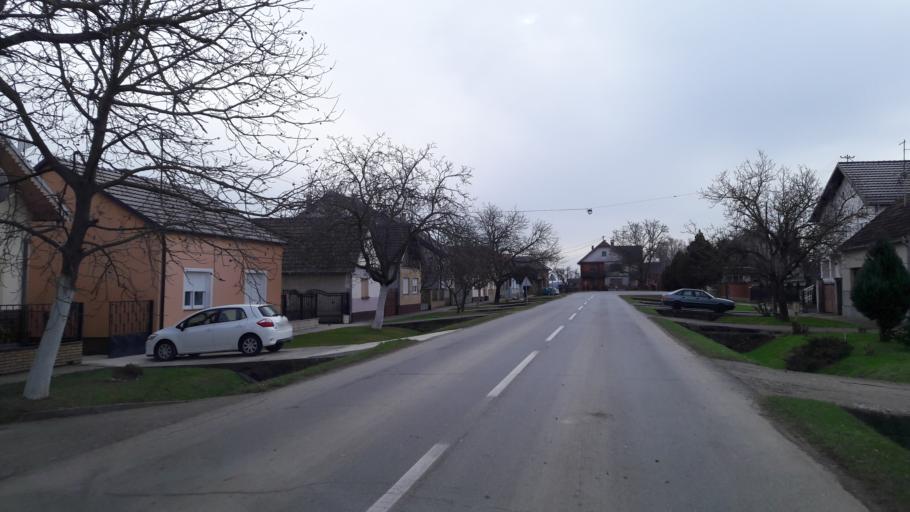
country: HR
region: Osjecko-Baranjska
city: Semeljci
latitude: 45.3833
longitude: 18.5628
